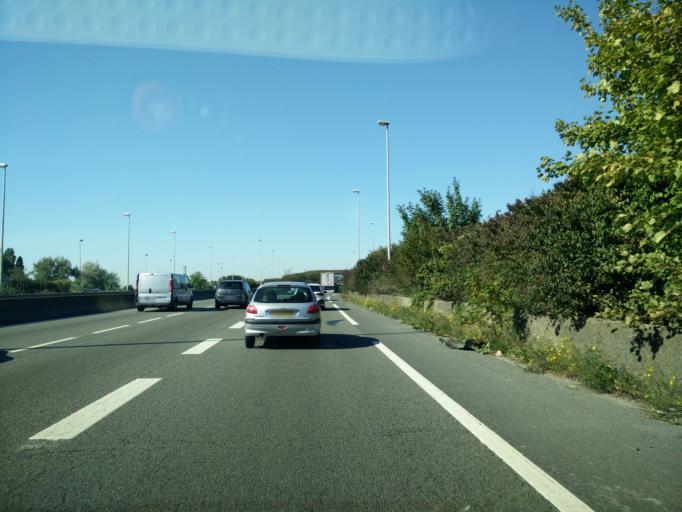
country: FR
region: Ile-de-France
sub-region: Departement de Seine-Saint-Denis
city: Aulnay-sous-Bois
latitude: 48.9727
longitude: 2.4941
